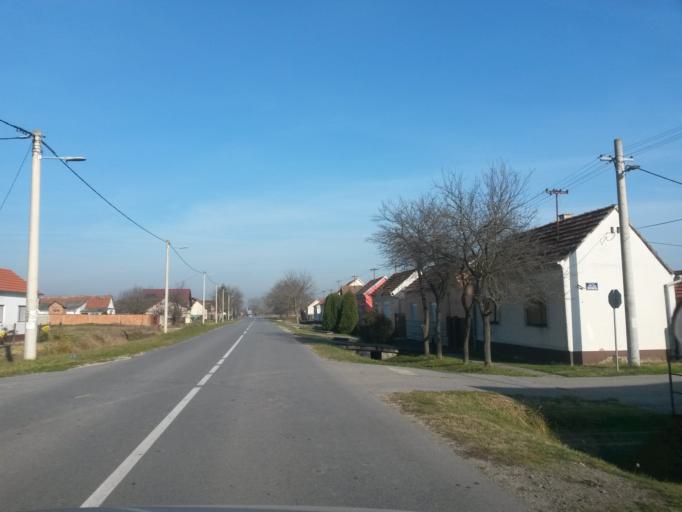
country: HR
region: Vukovarsko-Srijemska
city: Privlaka
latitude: 45.2059
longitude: 18.8518
